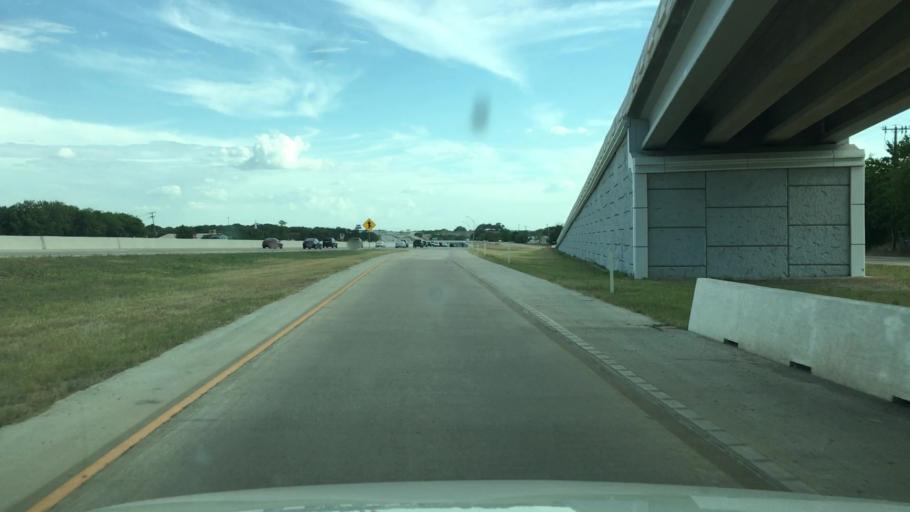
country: US
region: Texas
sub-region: Bell County
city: Salado
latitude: 30.9528
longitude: -97.5377
